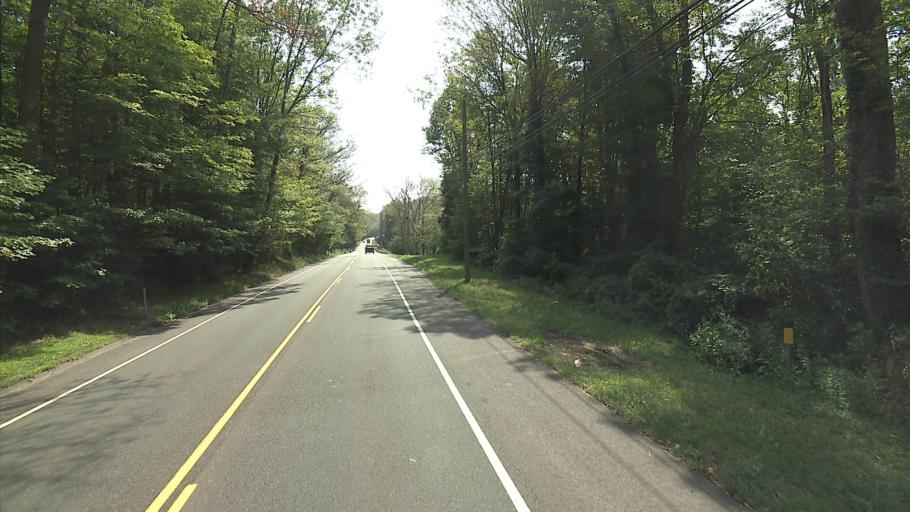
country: US
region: Connecticut
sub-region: Middlesex County
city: Durham
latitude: 41.4528
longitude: -72.6698
